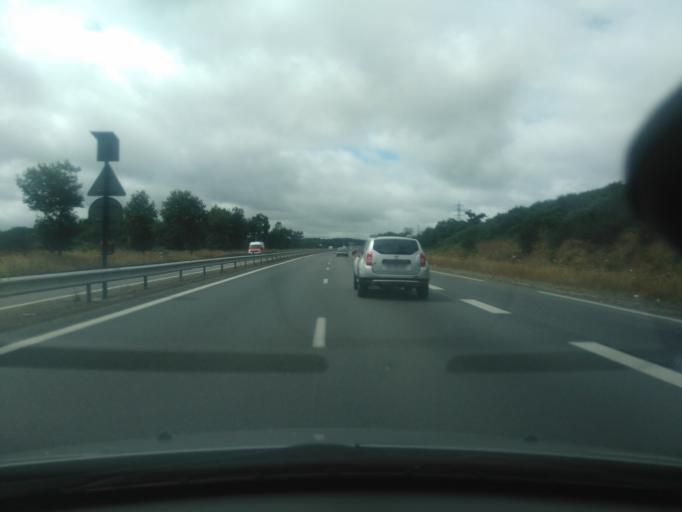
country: FR
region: Brittany
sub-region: Departement des Cotes-d'Armor
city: Ploufragan
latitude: 48.4759
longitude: -2.7698
